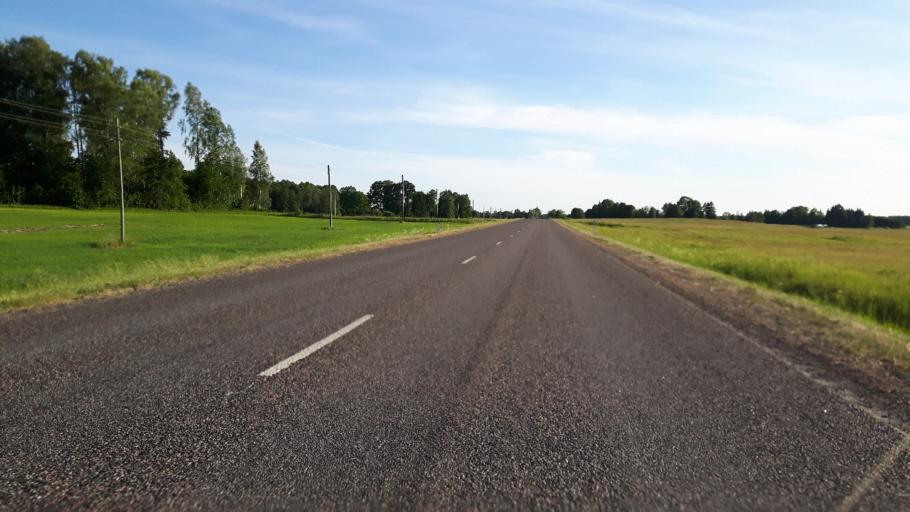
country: LV
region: Kuldigas Rajons
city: Kuldiga
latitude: 57.0087
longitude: 22.1490
